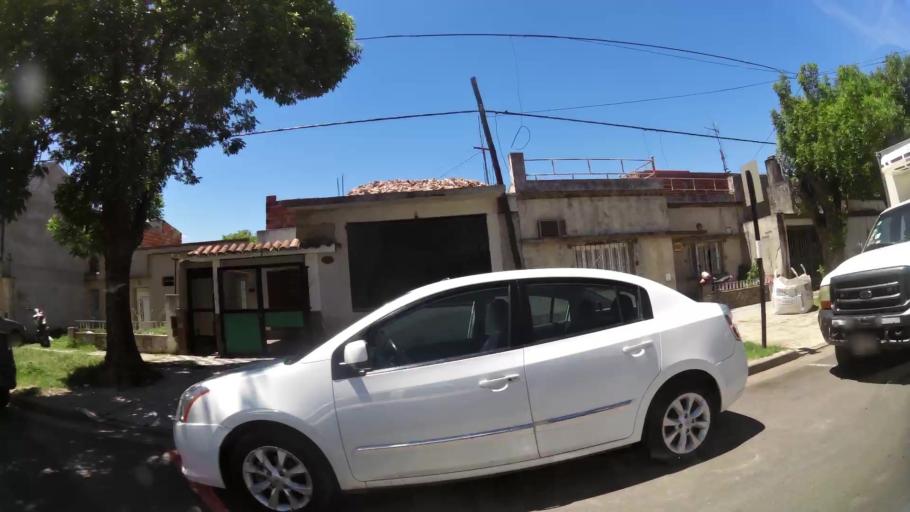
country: AR
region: Santa Fe
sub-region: Departamento de Rosario
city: Rosario
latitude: -32.9506
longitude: -60.7098
